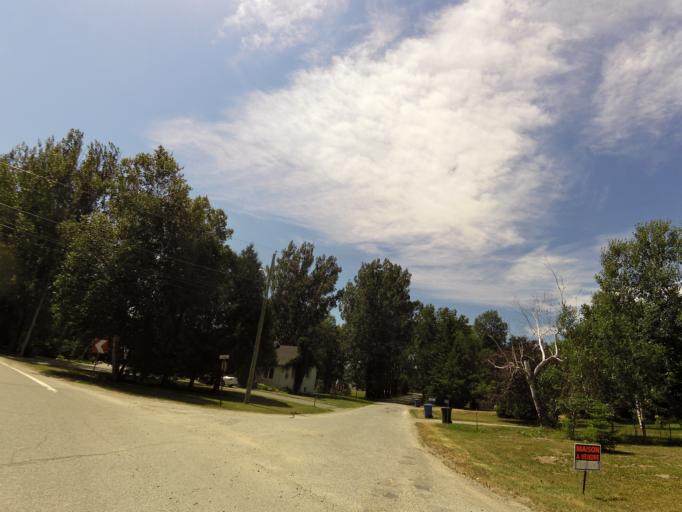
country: CA
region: Quebec
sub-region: Abitibi-Temiscamingue
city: Ville-Marie
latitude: 47.2942
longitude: -79.4377
